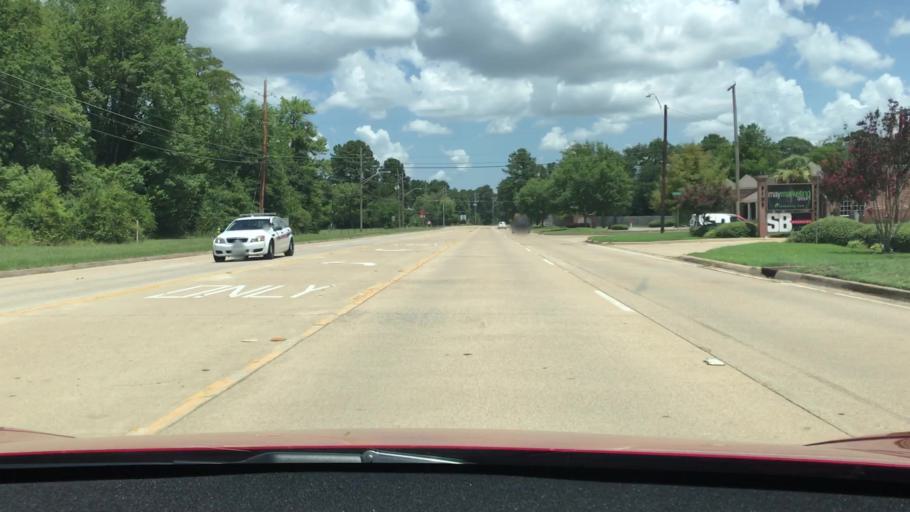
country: US
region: Louisiana
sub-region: Bossier Parish
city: Bossier City
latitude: 32.4099
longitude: -93.7385
